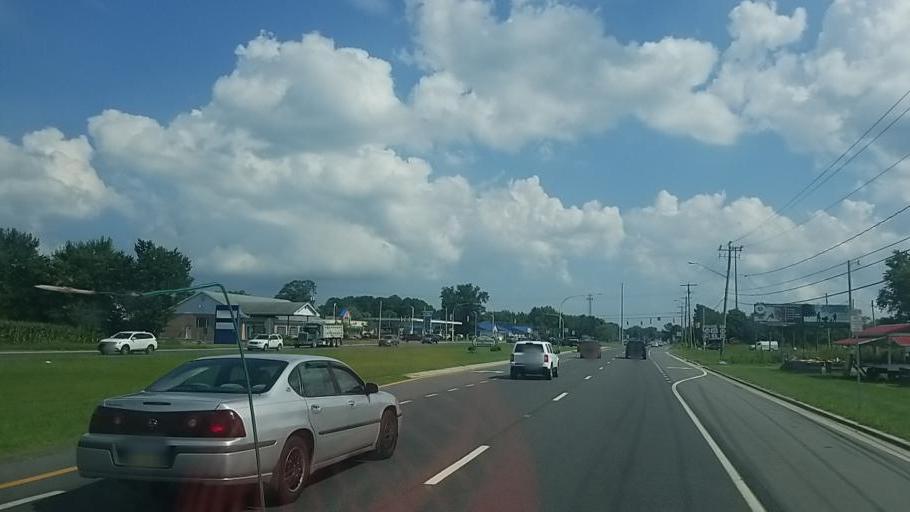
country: US
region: Delaware
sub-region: Sussex County
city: Millsboro
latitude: 38.5436
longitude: -75.2592
